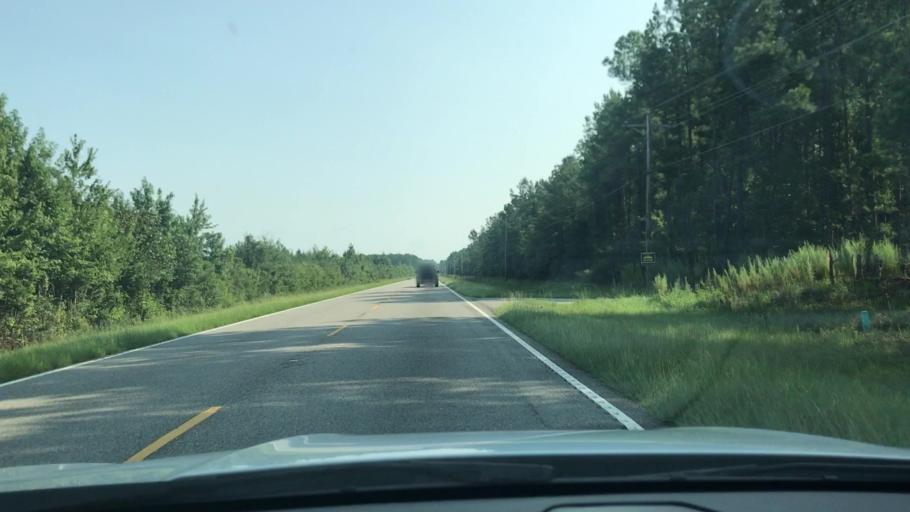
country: US
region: South Carolina
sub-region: Georgetown County
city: Georgetown
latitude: 33.5136
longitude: -79.2502
